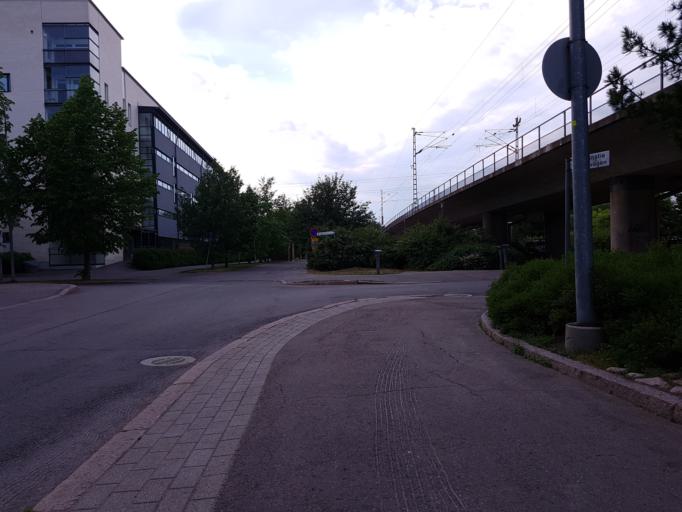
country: FI
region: Uusimaa
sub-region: Helsinki
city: Teekkarikylae
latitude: 60.2412
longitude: 24.8716
